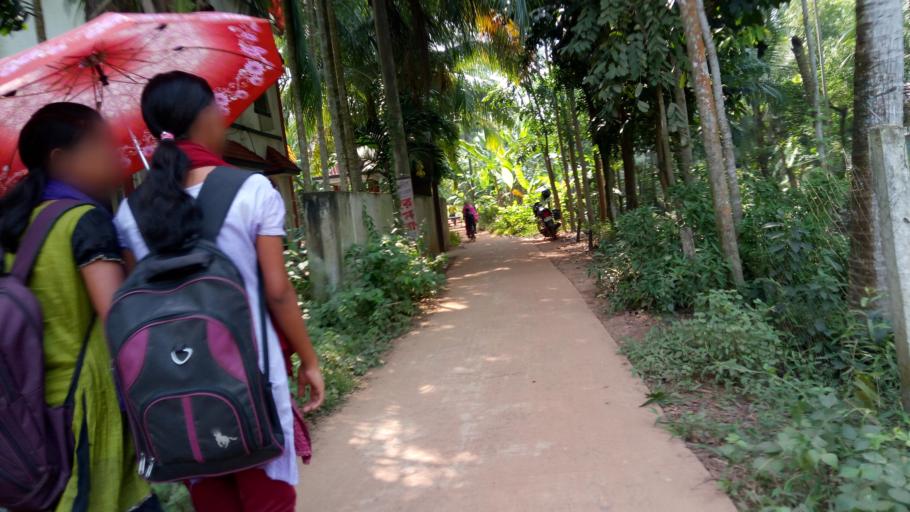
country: IN
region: West Bengal
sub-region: Purba Medinipur
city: Mahishadal
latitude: 22.1734
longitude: 87.9117
